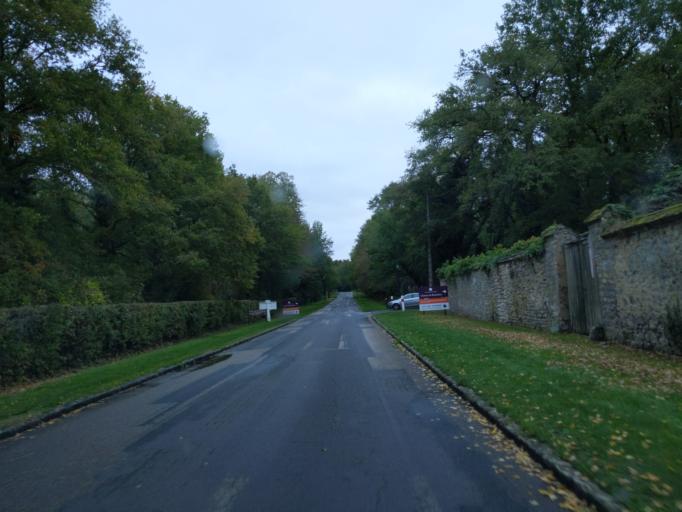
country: FR
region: Ile-de-France
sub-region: Departement des Yvelines
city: Bullion
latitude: 48.5892
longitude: 1.9903
